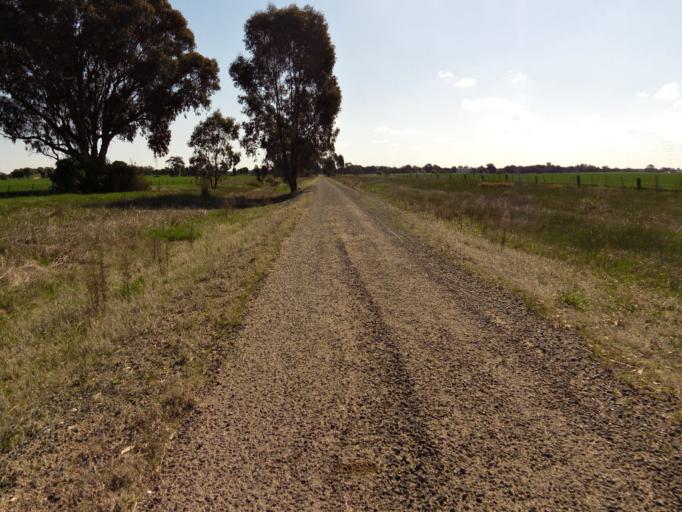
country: AU
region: New South Wales
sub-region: Corowa Shire
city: Corowa
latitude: -36.0190
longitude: 146.4195
